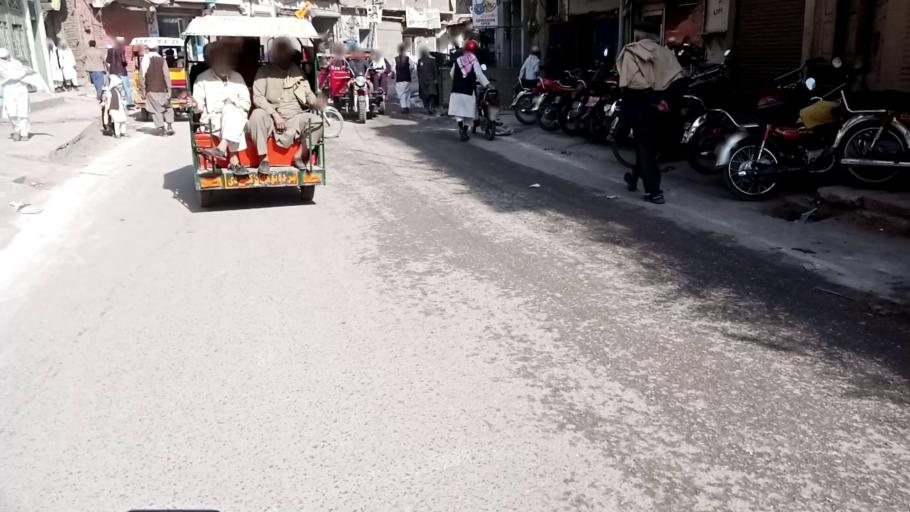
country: PK
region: Khyber Pakhtunkhwa
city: Peshawar
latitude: 34.0018
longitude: 71.5781
